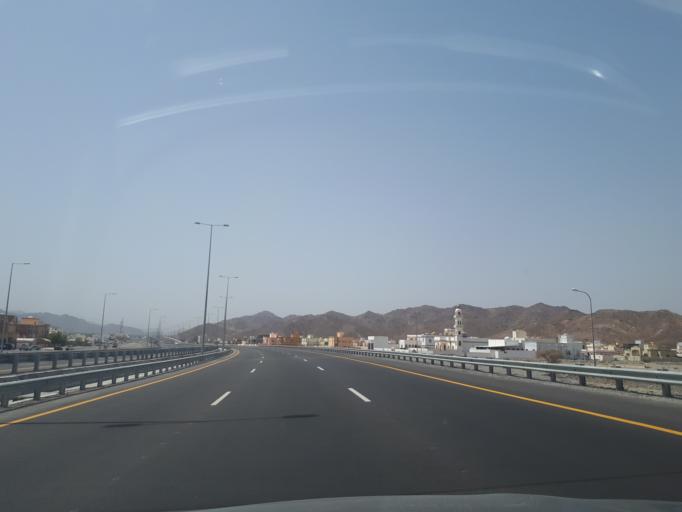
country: OM
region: Muhafazat ad Dakhiliyah
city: Bidbid
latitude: 23.4032
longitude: 58.0980
